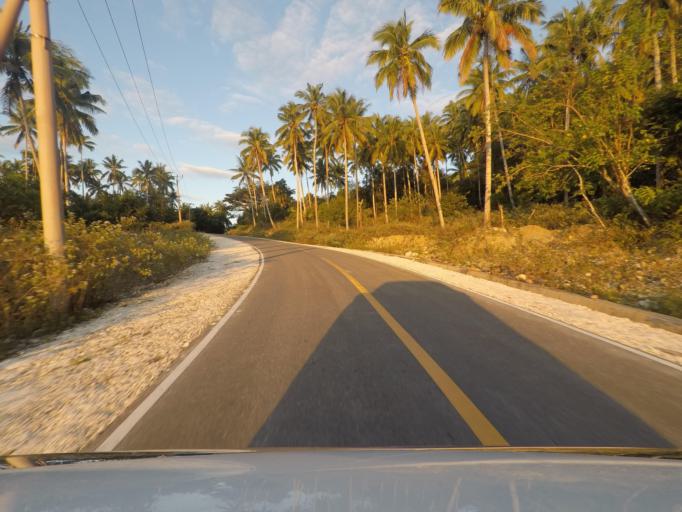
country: TL
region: Lautem
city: Lospalos
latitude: -8.3981
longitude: 127.2729
